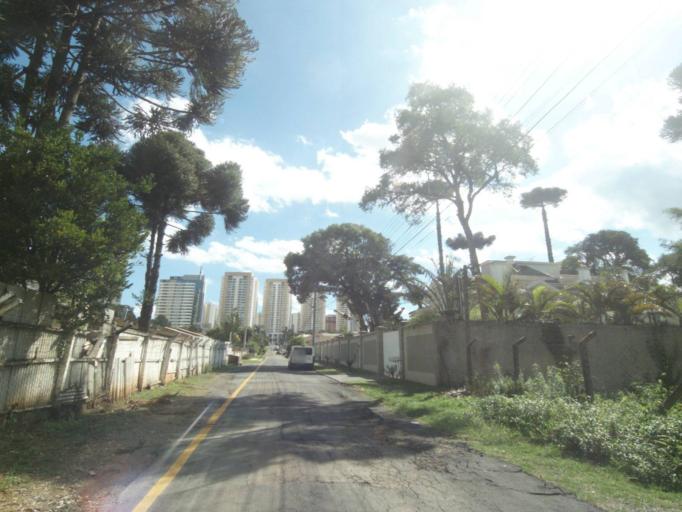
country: BR
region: Parana
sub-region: Curitiba
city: Curitiba
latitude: -25.4376
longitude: -49.3443
